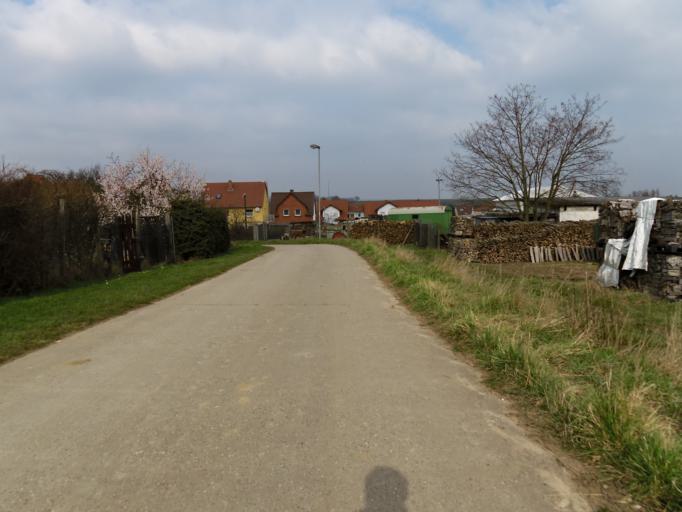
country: DE
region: Rheinland-Pfalz
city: Heidesheim
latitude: 49.5802
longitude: 8.1832
